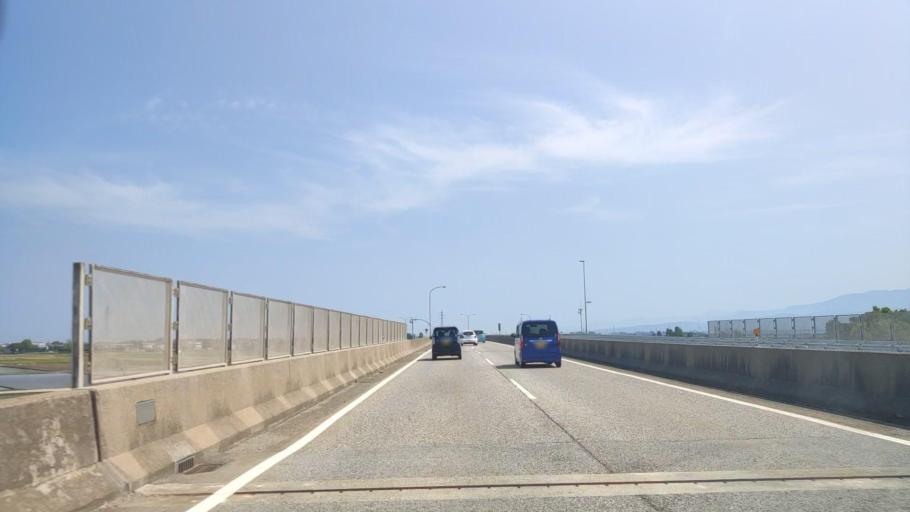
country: JP
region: Toyama
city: Namerikawa
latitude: 36.7405
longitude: 137.3422
